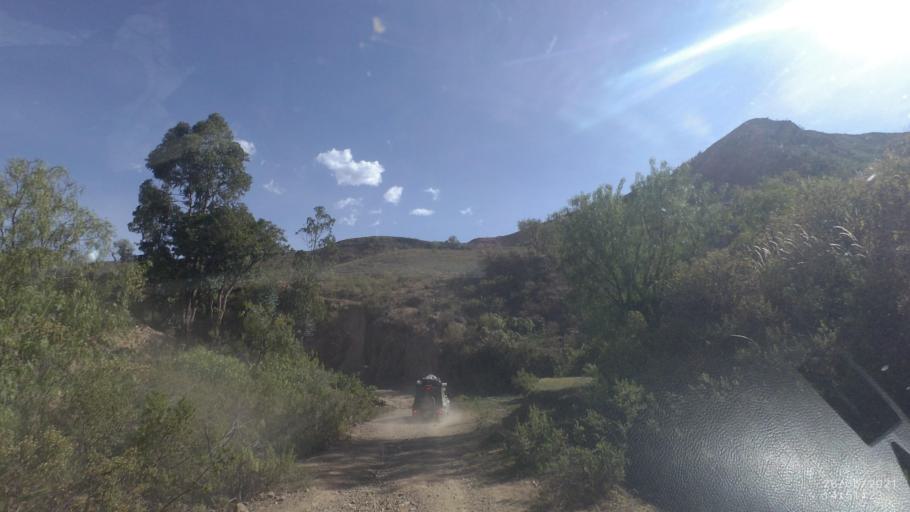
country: BO
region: Cochabamba
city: Mizque
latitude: -17.9238
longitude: -65.6274
